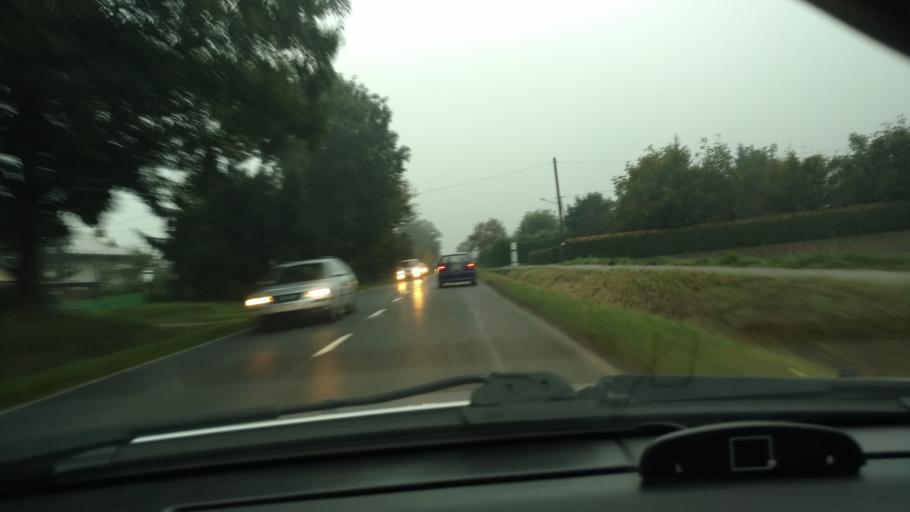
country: PL
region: Subcarpathian Voivodeship
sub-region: Powiat strzyzowski
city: Wysoka Strzyzowska
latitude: 49.8771
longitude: 21.7310
